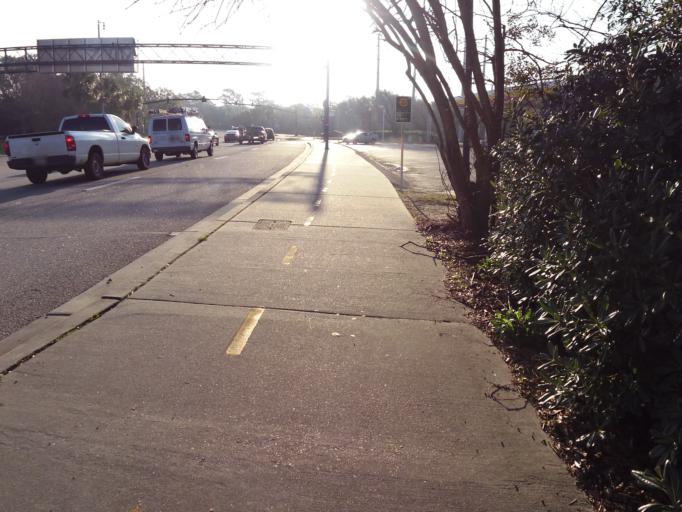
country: US
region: South Carolina
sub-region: Charleston County
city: Mount Pleasant
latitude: 32.7979
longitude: -79.8979
